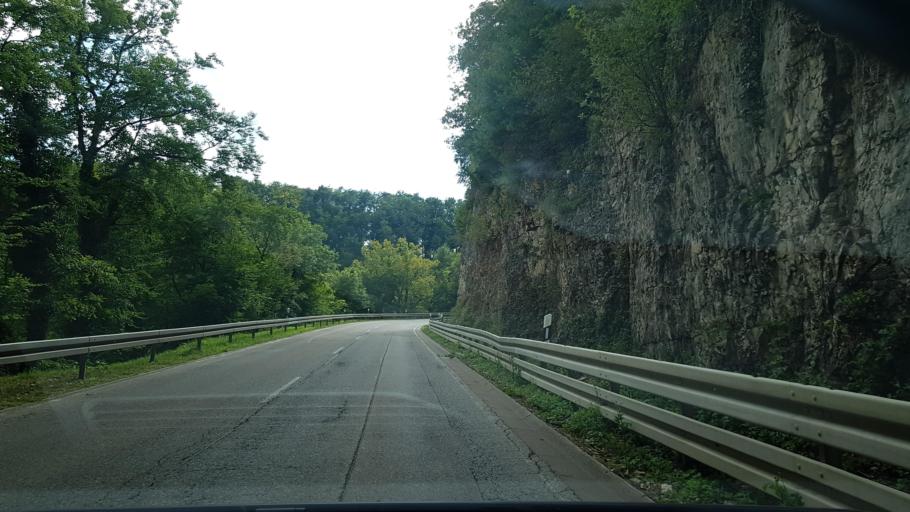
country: DE
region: Baden-Wuerttemberg
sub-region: Tuebingen Region
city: Grabenstetten
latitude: 48.5275
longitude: 9.4814
